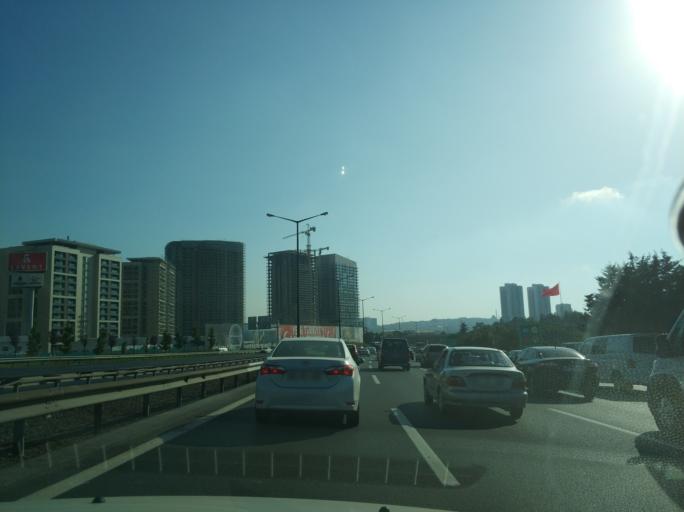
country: TR
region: Istanbul
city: Sisli
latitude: 41.0940
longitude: 28.9494
